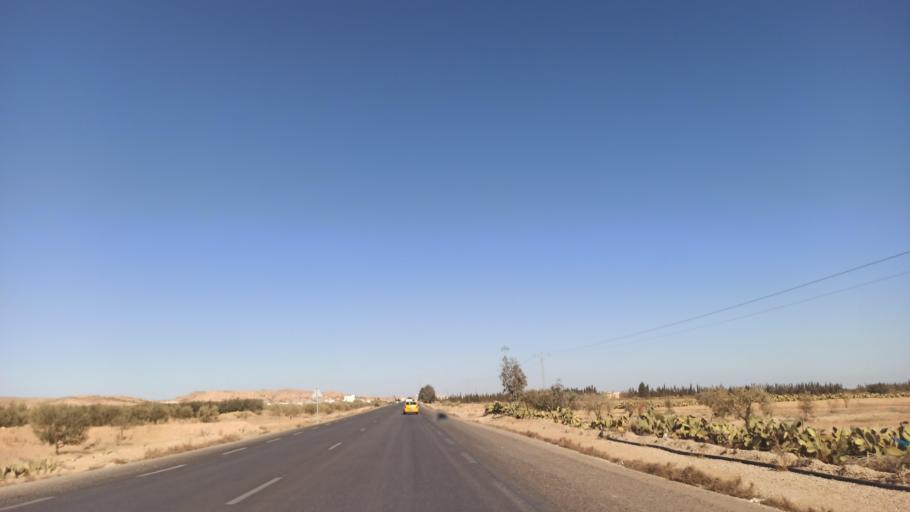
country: TN
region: Sidi Bu Zayd
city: Bi'r al Hufayy
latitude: 34.9045
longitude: 9.1775
